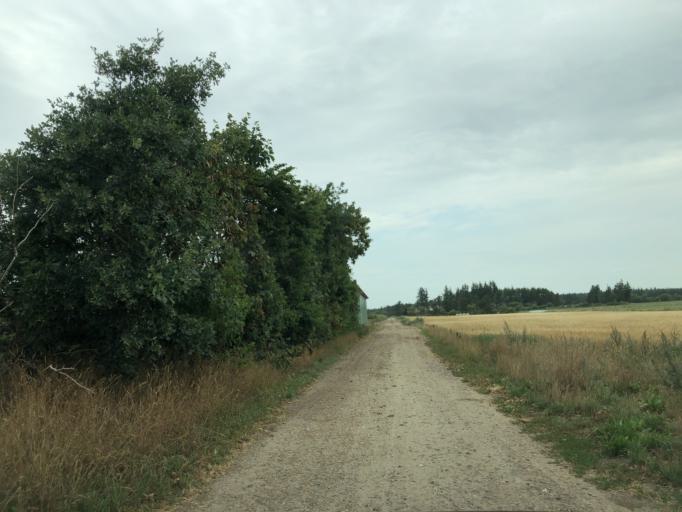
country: DK
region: Central Jutland
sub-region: Holstebro Kommune
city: Ulfborg
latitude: 56.2335
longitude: 8.3581
